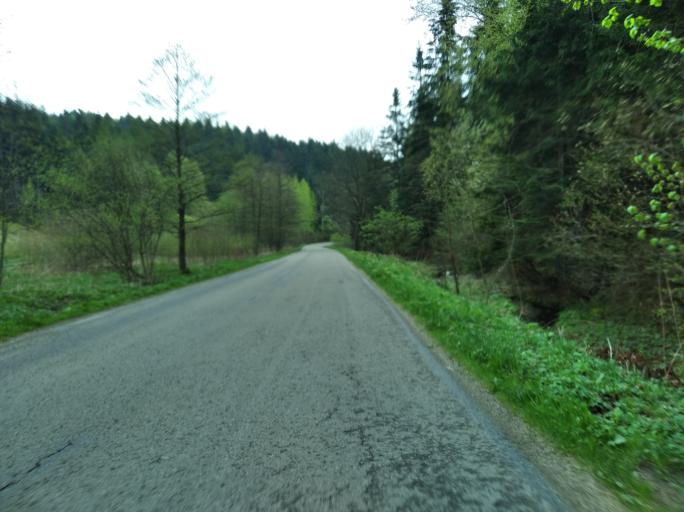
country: PL
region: Subcarpathian Voivodeship
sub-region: Powiat brzozowski
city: Golcowa
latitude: 49.7493
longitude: 22.0712
